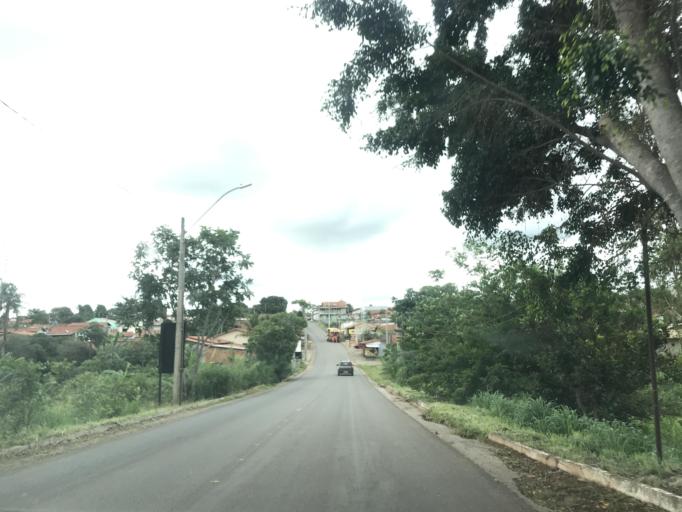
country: BR
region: Goias
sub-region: Bela Vista De Goias
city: Bela Vista de Goias
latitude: -17.0592
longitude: -48.6614
